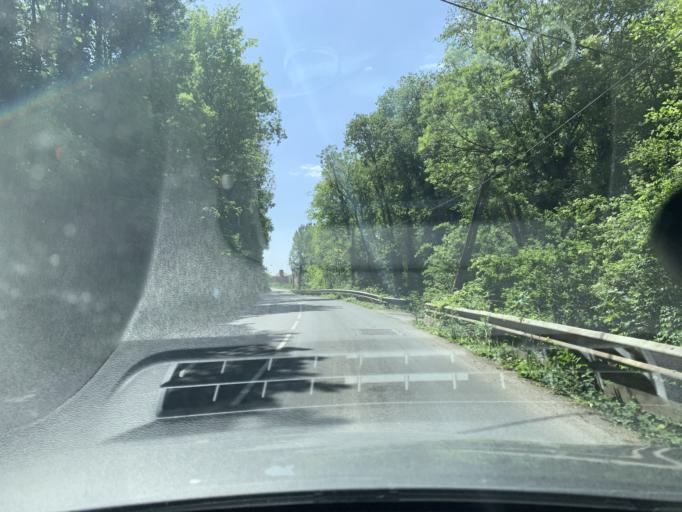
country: FR
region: Nord-Pas-de-Calais
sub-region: Departement du Nord
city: Marcoing
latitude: 50.1256
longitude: 3.1872
